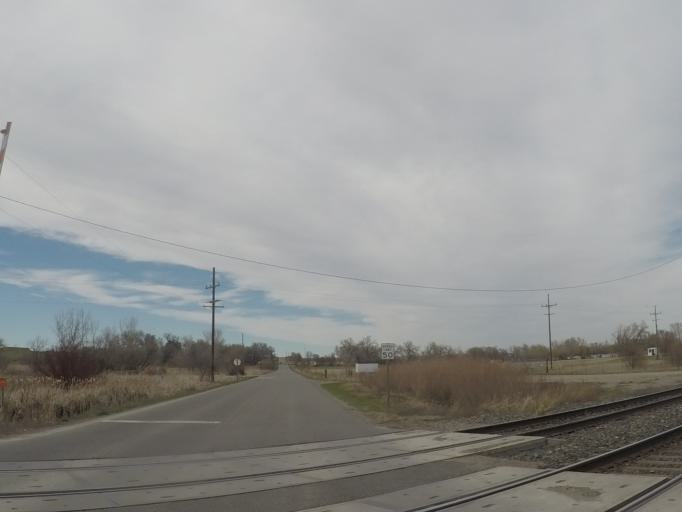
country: US
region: Montana
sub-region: Yellowstone County
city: Laurel
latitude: 45.7062
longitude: -108.6587
